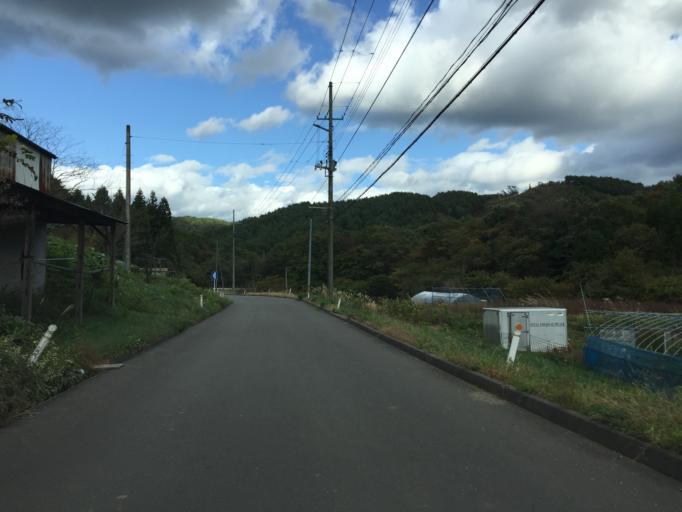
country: JP
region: Miyagi
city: Marumori
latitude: 37.8204
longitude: 140.7657
